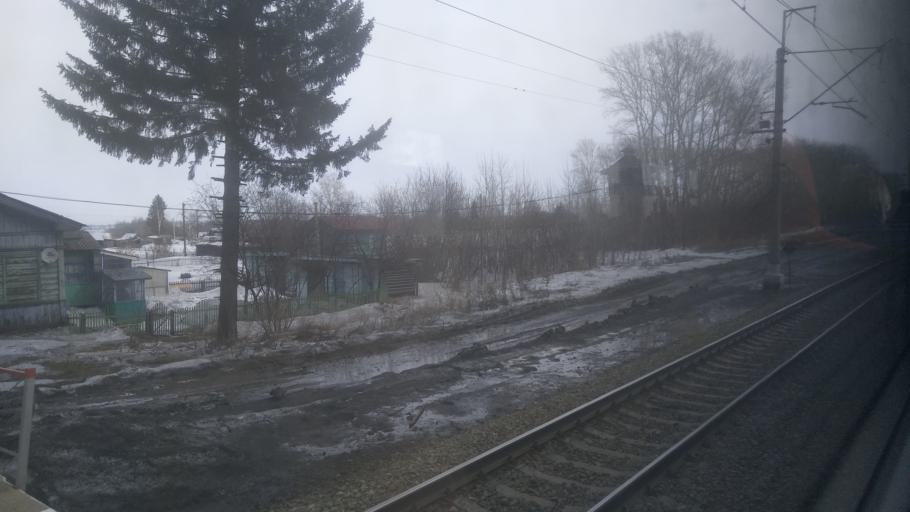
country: RU
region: Kemerovo
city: Yurga
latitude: 55.6984
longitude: 84.6535
